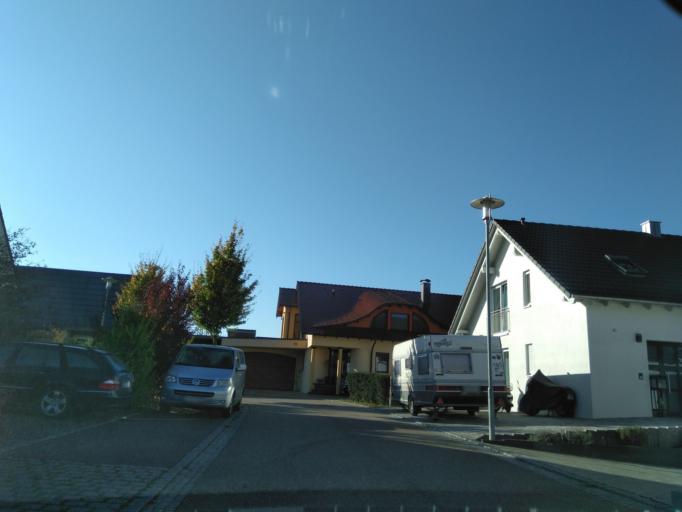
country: DE
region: Baden-Wuerttemberg
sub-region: Regierungsbezirk Stuttgart
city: Markgroningen
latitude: 48.8962
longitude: 9.0934
